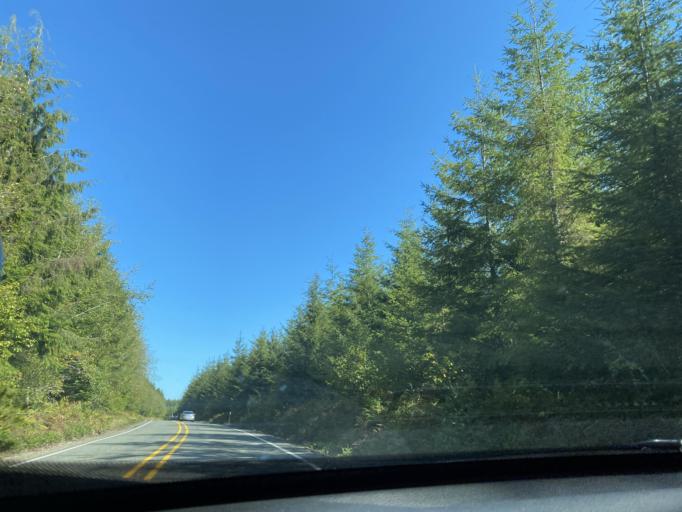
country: US
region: Washington
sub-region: Clallam County
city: Forks
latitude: 47.9378
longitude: -124.4681
